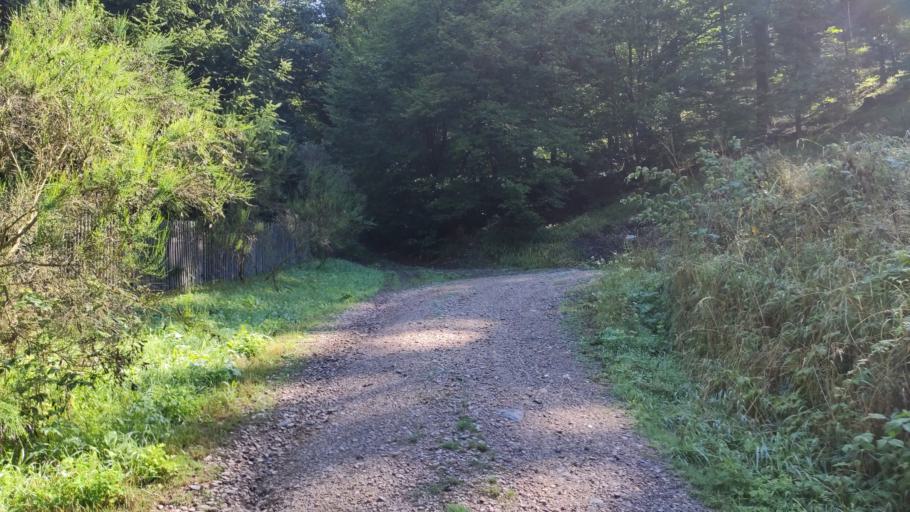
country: DE
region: Thuringia
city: Leutenberg
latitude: 50.5796
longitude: 11.4519
